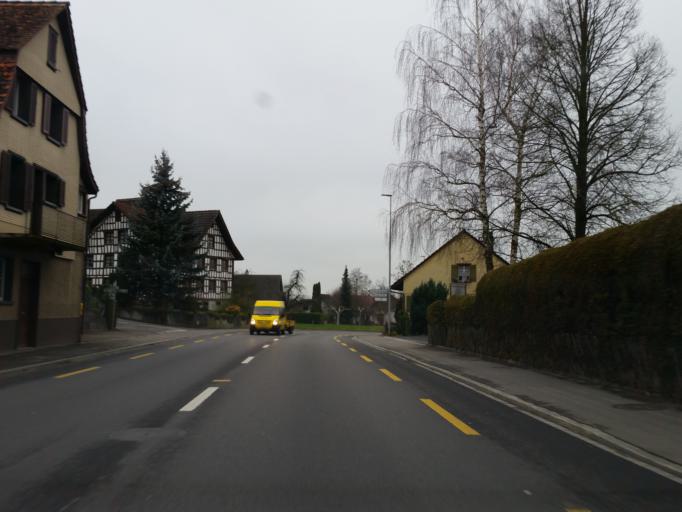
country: CH
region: Thurgau
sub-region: Weinfelden District
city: Erlen
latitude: 47.5463
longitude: 9.2419
